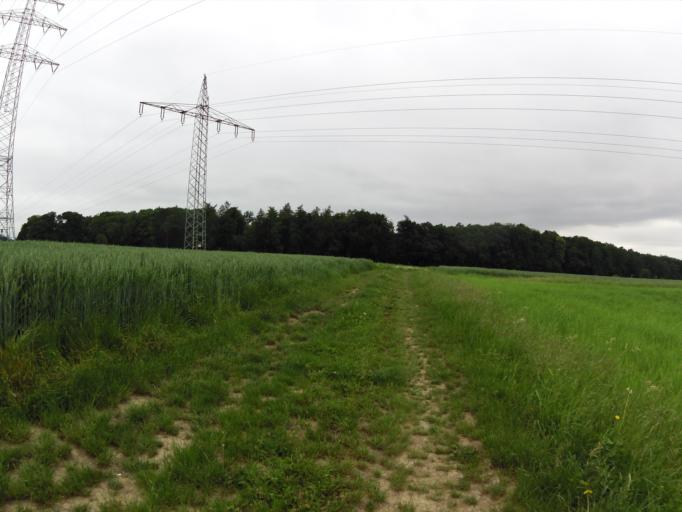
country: DE
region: Bavaria
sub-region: Regierungsbezirk Unterfranken
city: Zell am Main
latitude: 49.8155
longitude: 9.8533
